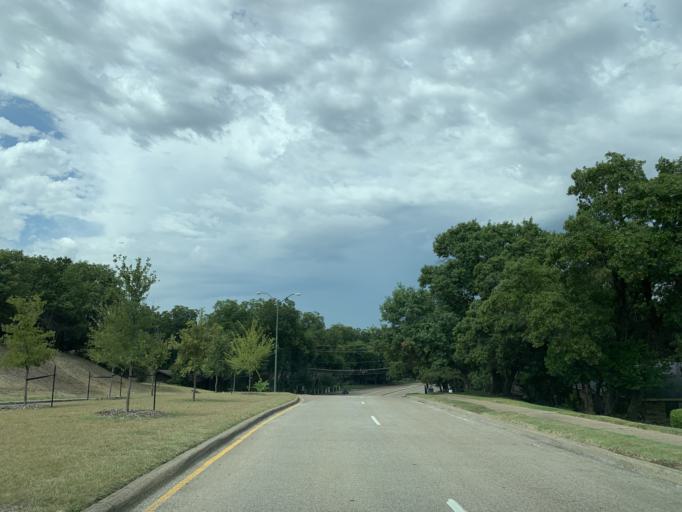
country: US
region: Texas
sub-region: Dallas County
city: Duncanville
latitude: 32.6734
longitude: -96.8348
